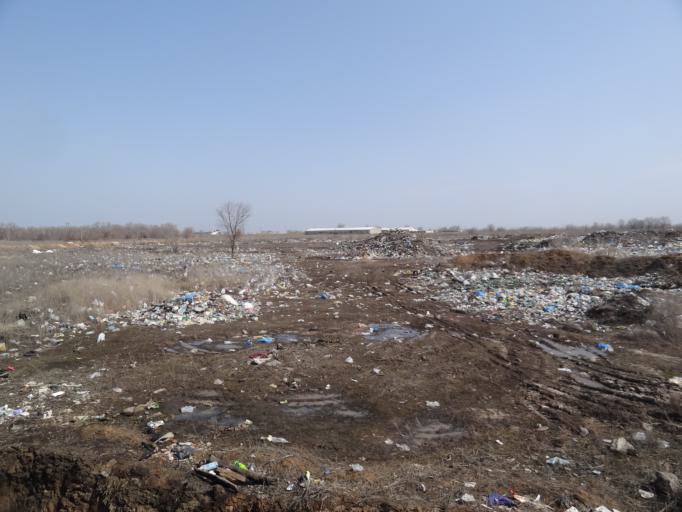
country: RU
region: Saratov
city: Engel's
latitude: 51.4223
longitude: 46.1800
